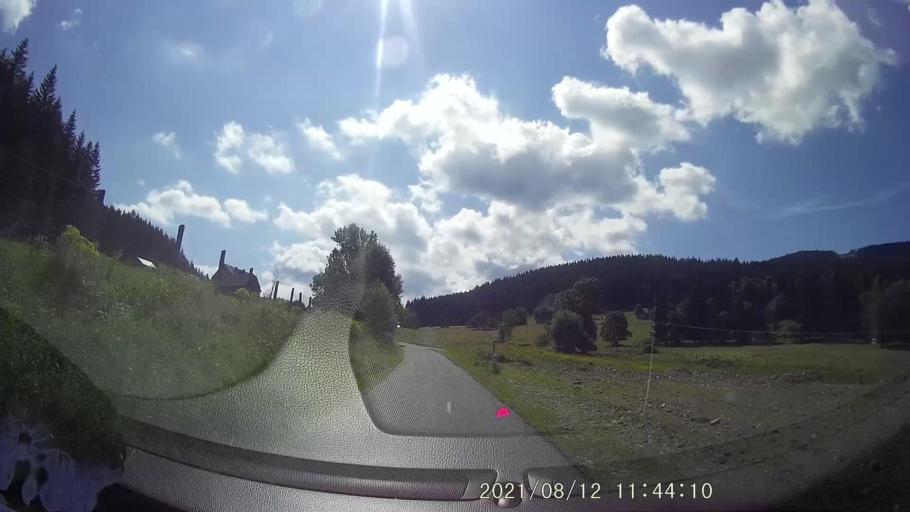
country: PL
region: Lower Silesian Voivodeship
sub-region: Powiat klodzki
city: Stronie Slaskie
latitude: 50.2577
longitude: 16.8356
